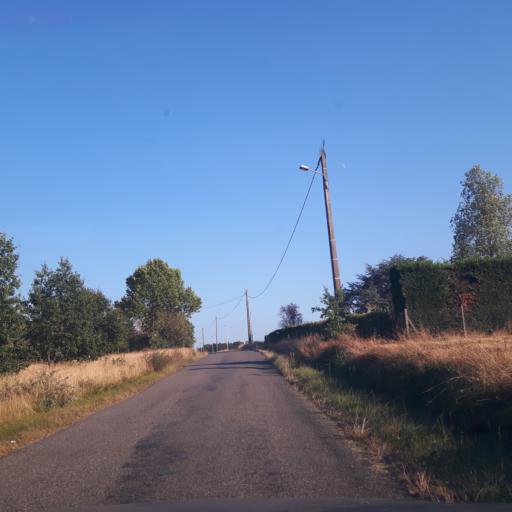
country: FR
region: Midi-Pyrenees
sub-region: Departement de la Haute-Garonne
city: Villaudric
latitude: 43.8020
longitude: 1.4440
